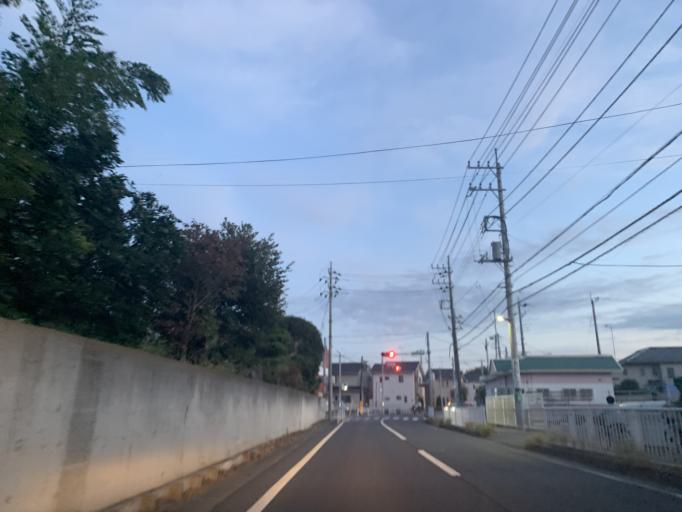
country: JP
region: Chiba
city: Nagareyama
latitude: 35.8924
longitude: 139.9254
